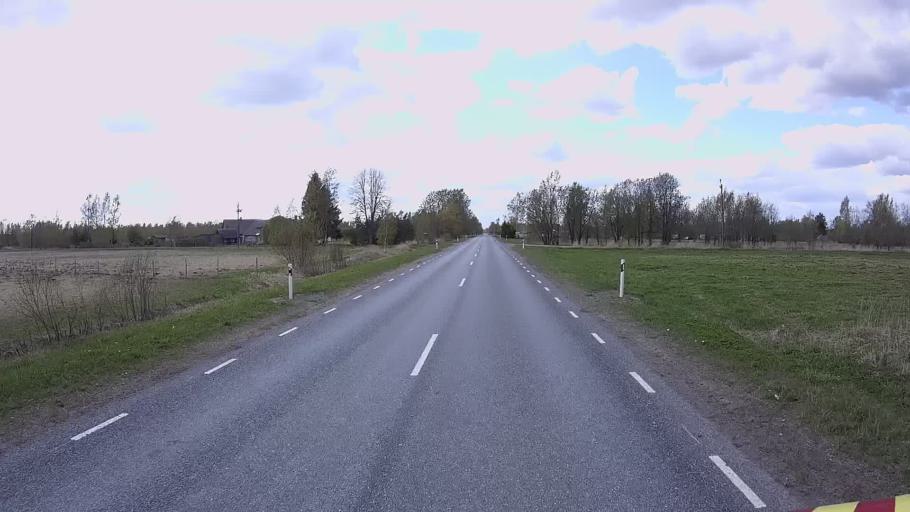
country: EE
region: Jogevamaa
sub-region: Mustvee linn
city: Mustvee
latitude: 58.7853
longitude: 26.9670
